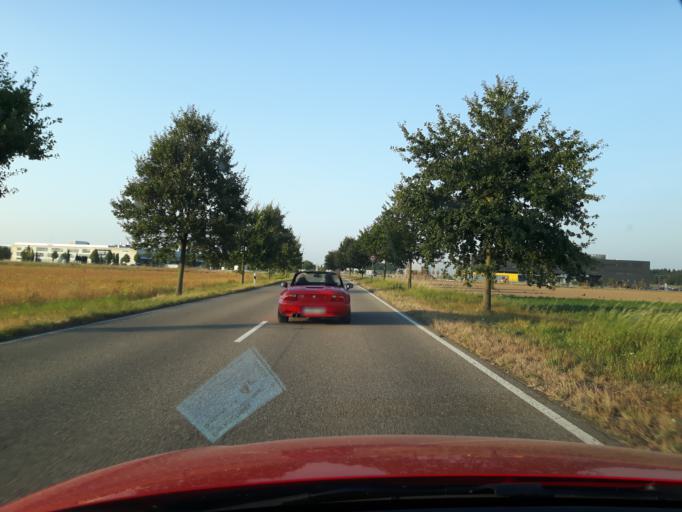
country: DE
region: Baden-Wuerttemberg
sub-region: Karlsruhe Region
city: Rheinstetten
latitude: 48.9736
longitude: 8.3348
